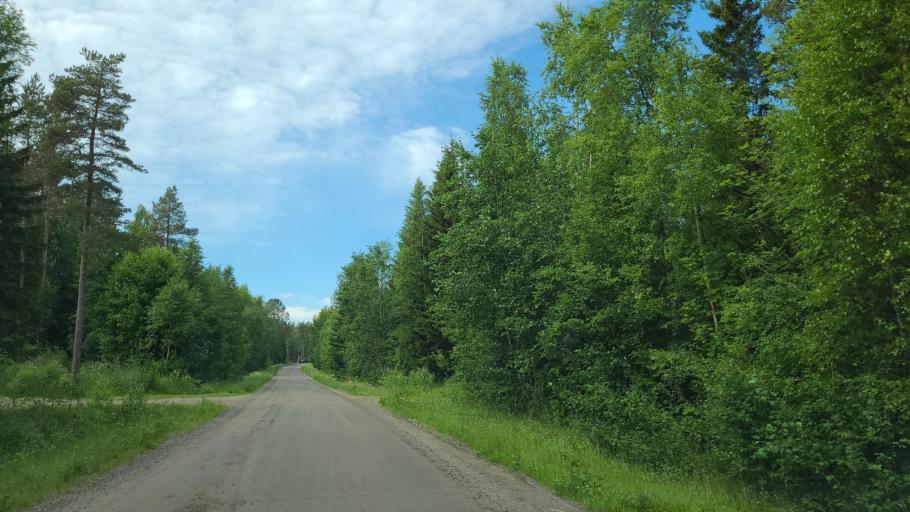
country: SE
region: Vaesterbotten
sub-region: Robertsfors Kommun
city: Robertsfors
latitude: 64.1650
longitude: 20.9696
